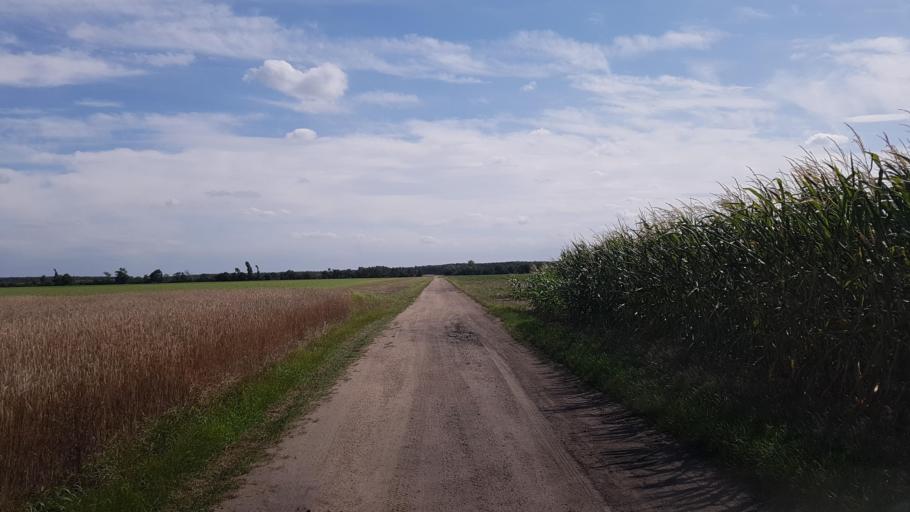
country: DE
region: Brandenburg
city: Muhlberg
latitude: 51.4608
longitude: 13.2828
